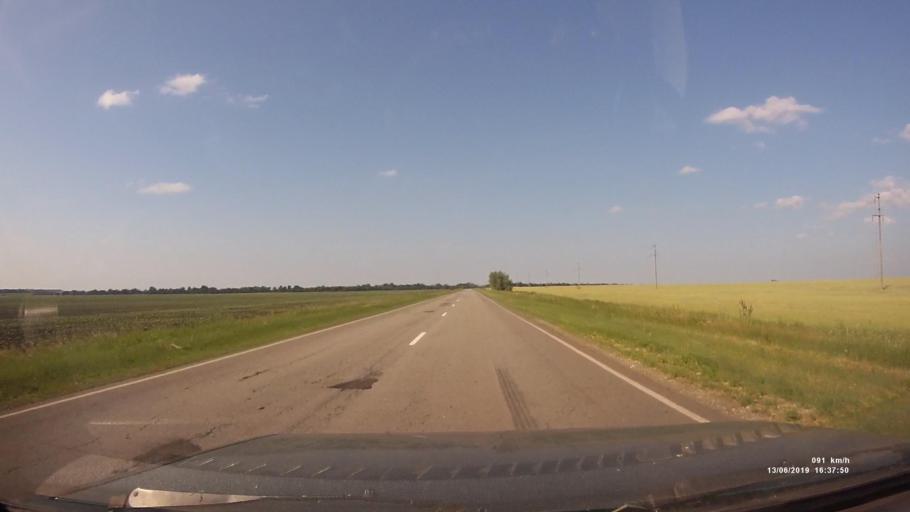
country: RU
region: Rostov
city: Kazanskaya
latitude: 49.9117
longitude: 41.3175
